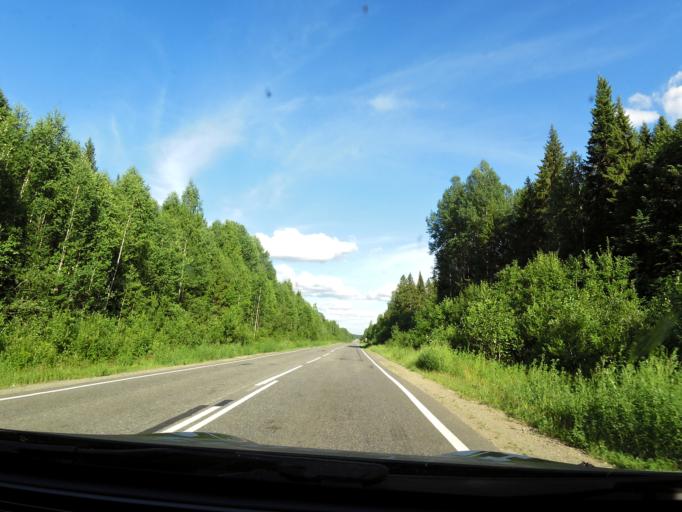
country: RU
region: Kirov
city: Omutninsk
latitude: 58.7615
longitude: 52.0053
